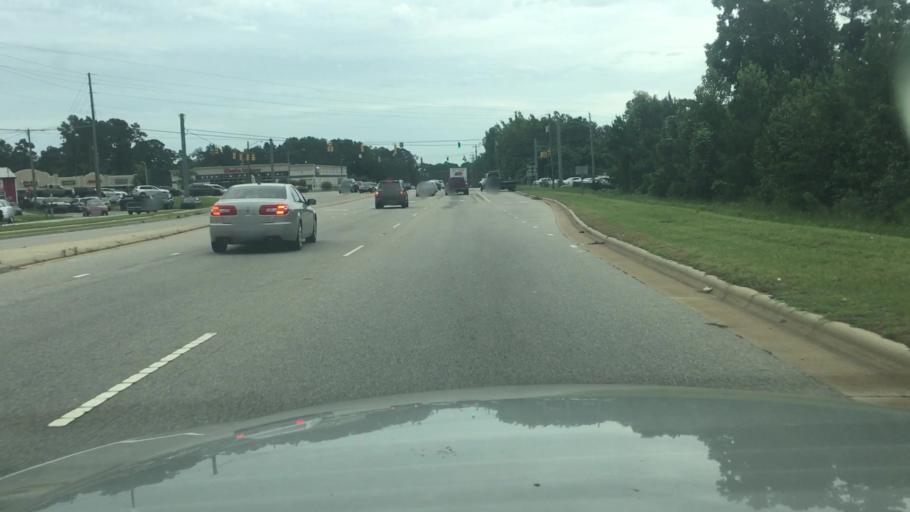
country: US
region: North Carolina
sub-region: Cumberland County
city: Hope Mills
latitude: 34.9963
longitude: -78.9691
